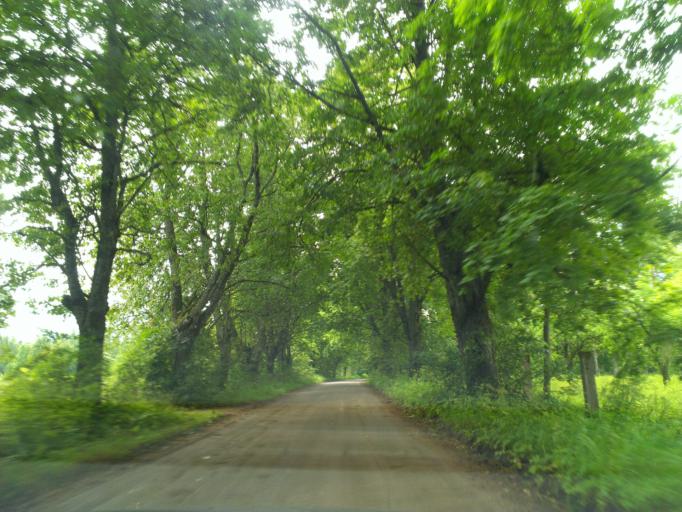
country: LV
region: Ligatne
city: Ligatne
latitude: 57.2129
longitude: 25.0195
